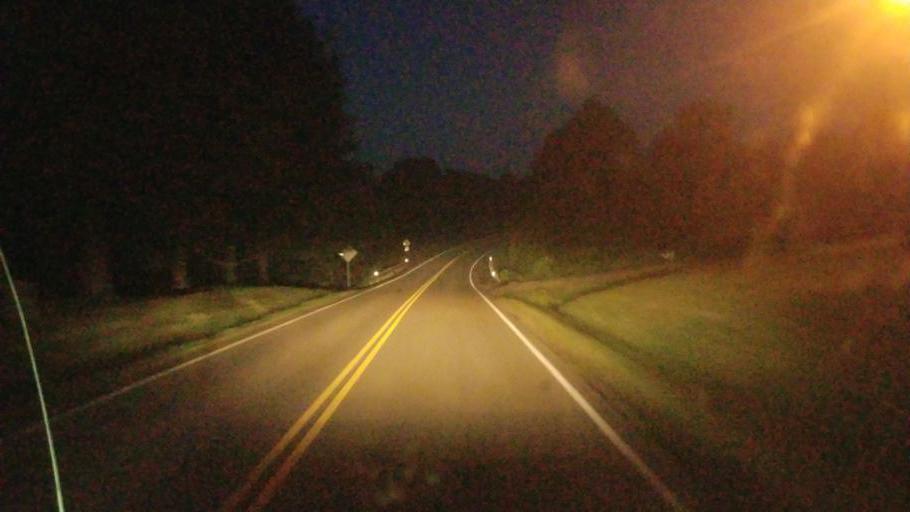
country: US
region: Ohio
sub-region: Perry County
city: Somerset
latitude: 39.8798
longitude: -82.3067
